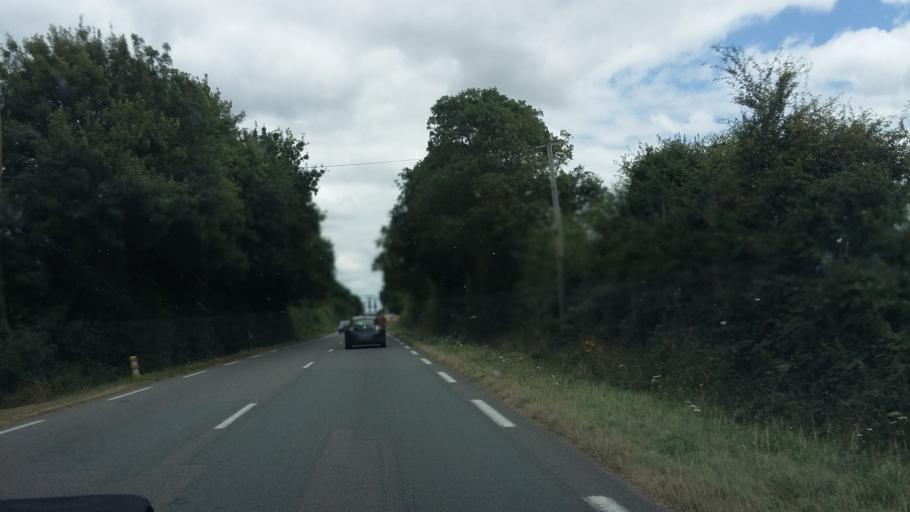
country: FR
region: Pays de la Loire
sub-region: Departement de la Vendee
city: Challans
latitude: 46.8337
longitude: -1.8259
